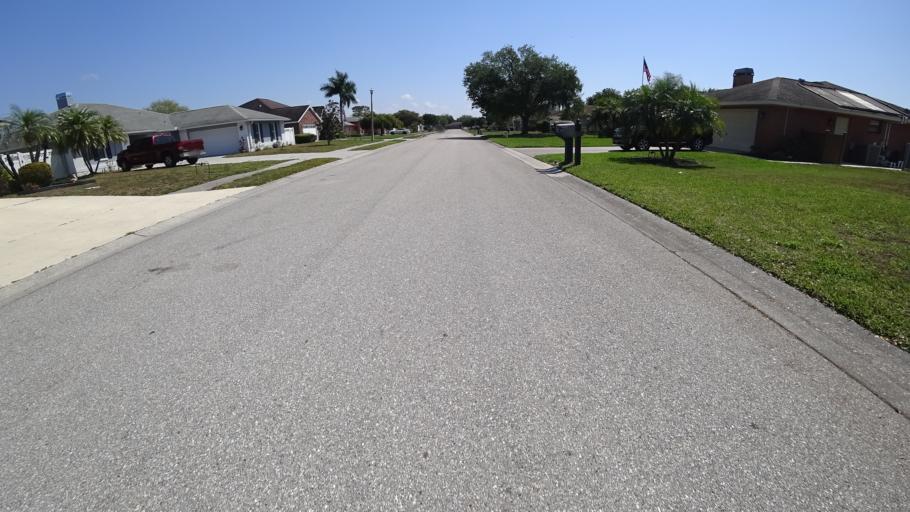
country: US
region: Florida
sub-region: Manatee County
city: Samoset
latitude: 27.4543
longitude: -82.5210
